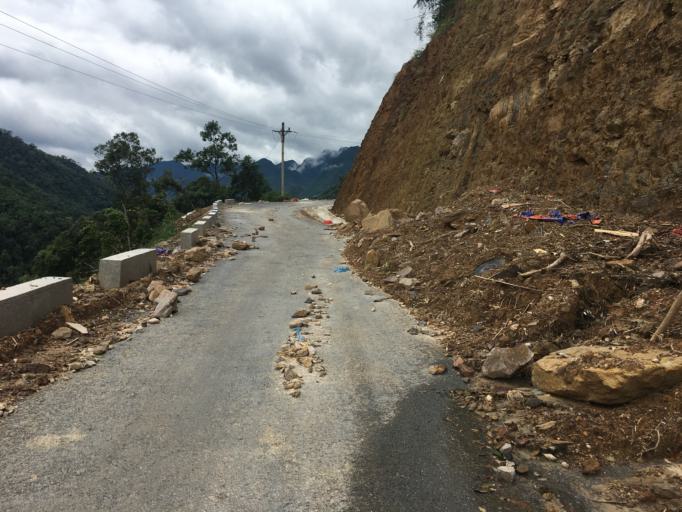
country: VN
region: Ha Giang
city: Thi Tran Tam Son
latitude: 22.9820
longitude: 105.0565
